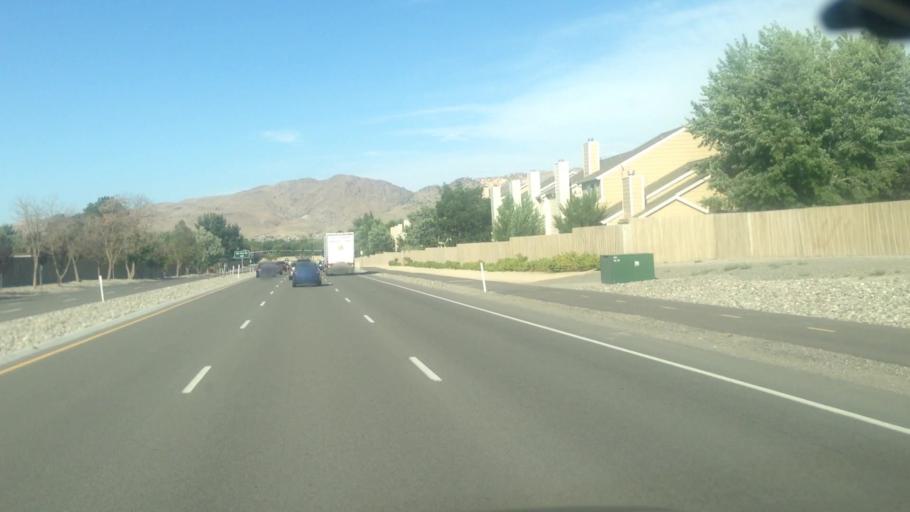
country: US
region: Nevada
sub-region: Washoe County
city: Sparks
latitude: 39.4775
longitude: -119.7585
